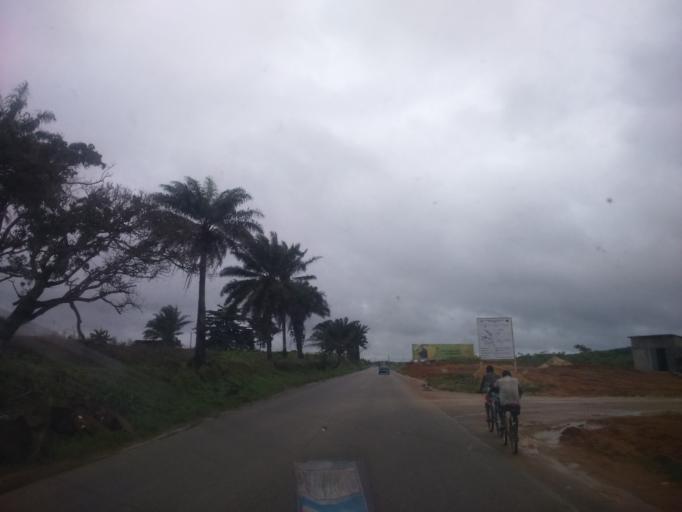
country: CI
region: Sud-Comoe
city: Bonoua
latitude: 5.2750
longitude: -3.5799
